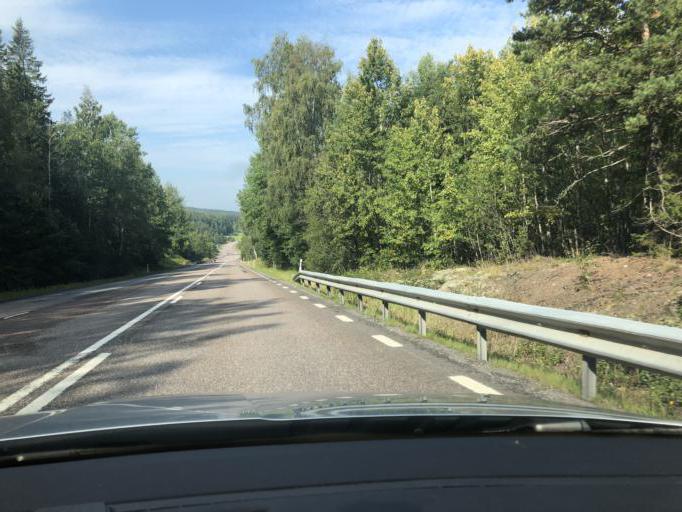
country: SE
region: Vaesternorrland
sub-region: Kramfors Kommun
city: Kramfors
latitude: 62.8157
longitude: 17.8622
